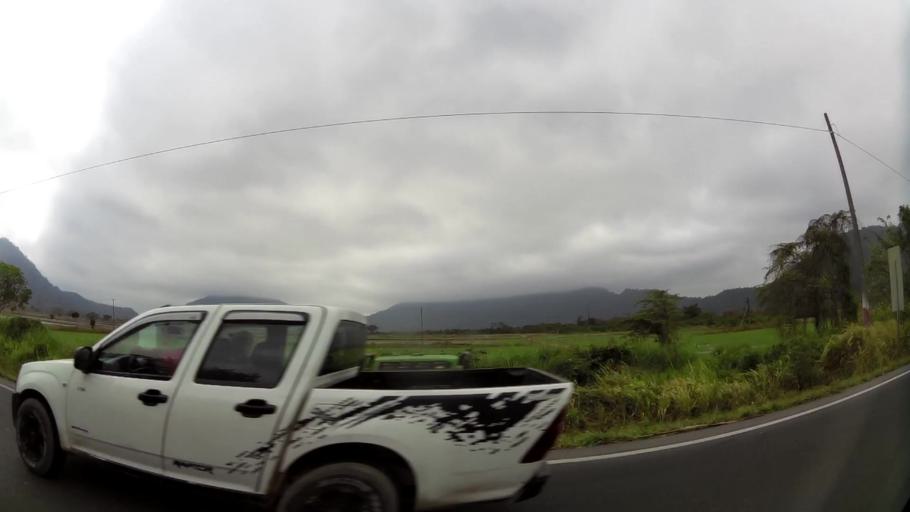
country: EC
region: Guayas
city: Naranjal
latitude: -2.4287
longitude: -79.6258
